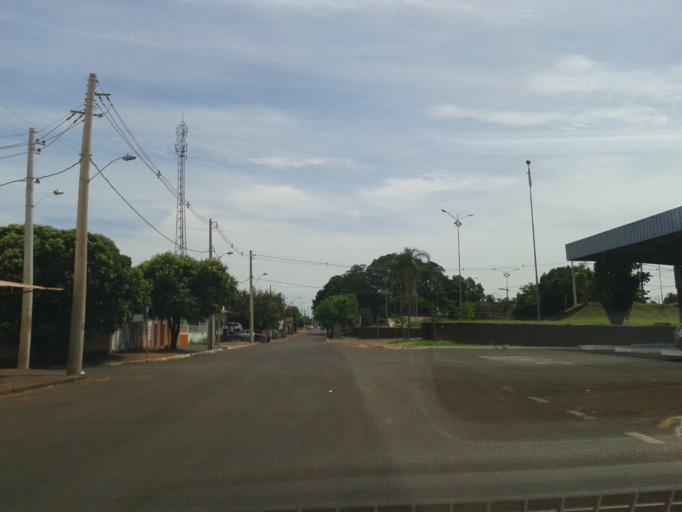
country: BR
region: Minas Gerais
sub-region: Santa Vitoria
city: Santa Vitoria
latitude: -18.8449
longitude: -50.1310
